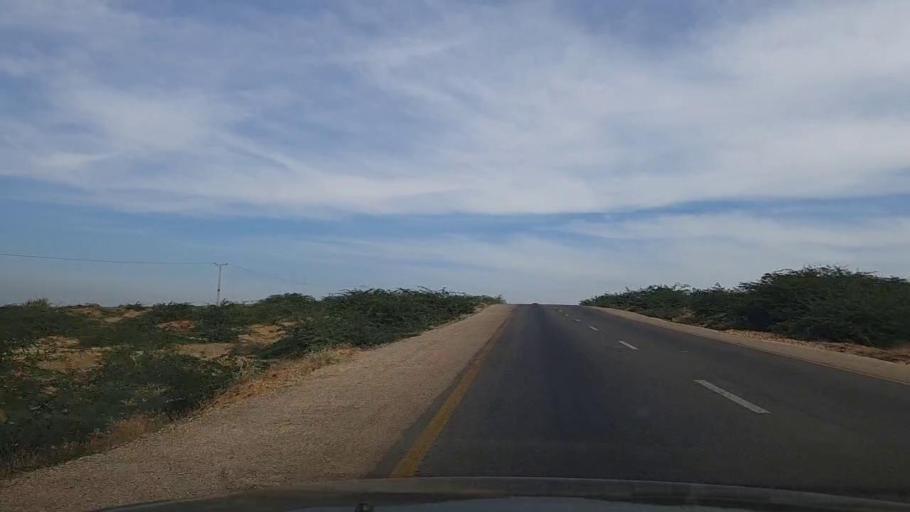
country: PK
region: Sindh
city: Thatta
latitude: 24.8492
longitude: 68.0141
